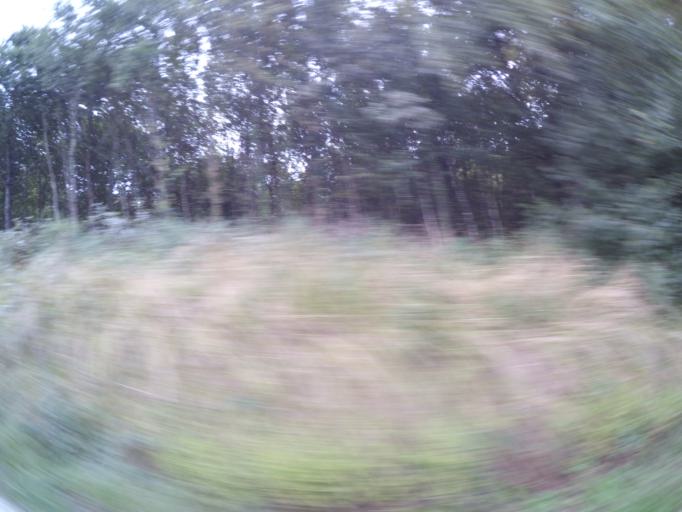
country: FR
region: Centre
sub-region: Departement d'Indre-et-Loire
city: Reugny
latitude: 47.4830
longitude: 0.9223
